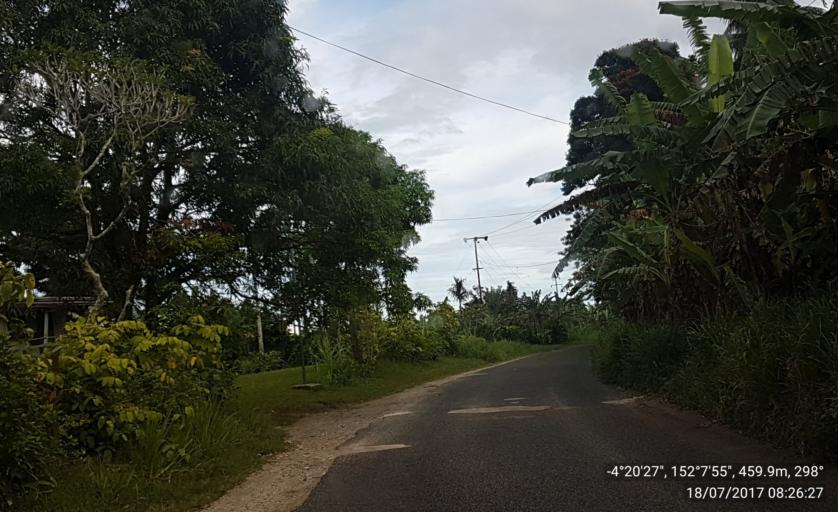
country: PG
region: East New Britain
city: Kokopo
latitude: -4.3408
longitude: 152.1322
